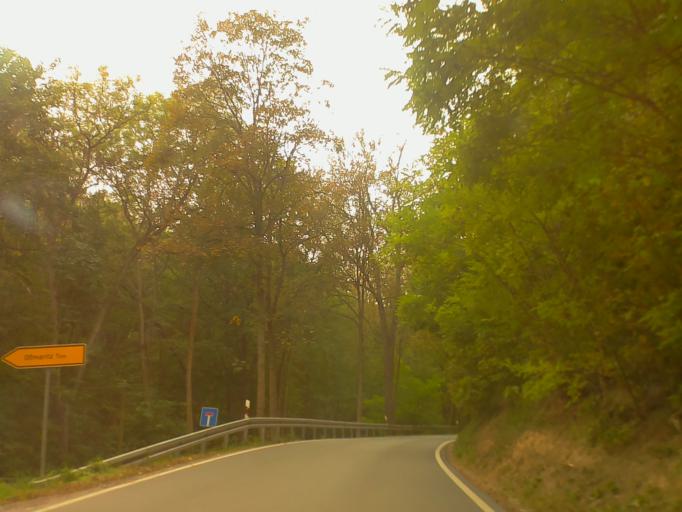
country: DE
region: Thuringia
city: Bucha
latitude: 50.8822
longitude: 11.5381
